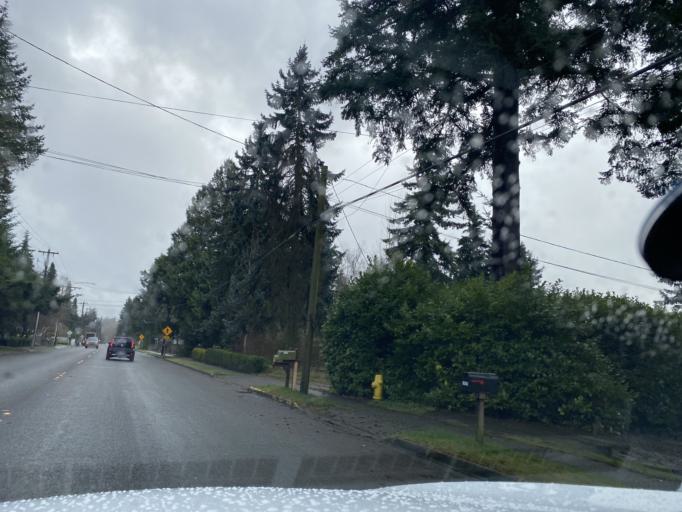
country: US
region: Washington
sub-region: Snohomish County
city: Lynnwood
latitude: 47.8267
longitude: -122.3034
